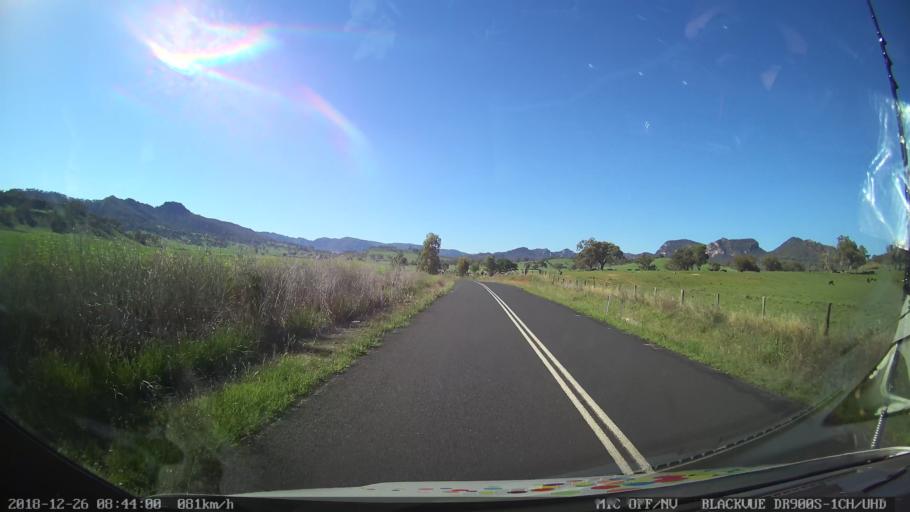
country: AU
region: New South Wales
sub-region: Mid-Western Regional
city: Kandos
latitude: -32.5089
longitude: 150.0803
